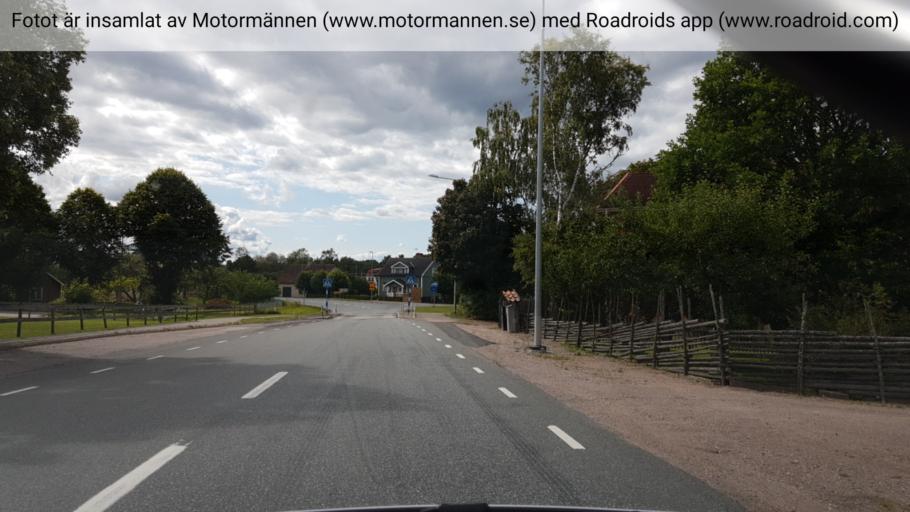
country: SE
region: Joenkoeping
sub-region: Tranas Kommun
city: Tranas
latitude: 57.9942
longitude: 14.8575
